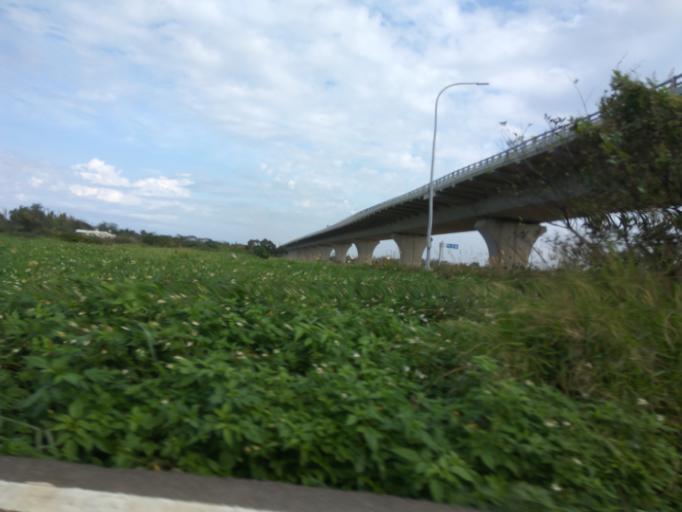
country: TW
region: Taiwan
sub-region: Hsinchu
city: Zhubei
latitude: 24.9640
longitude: 121.0124
